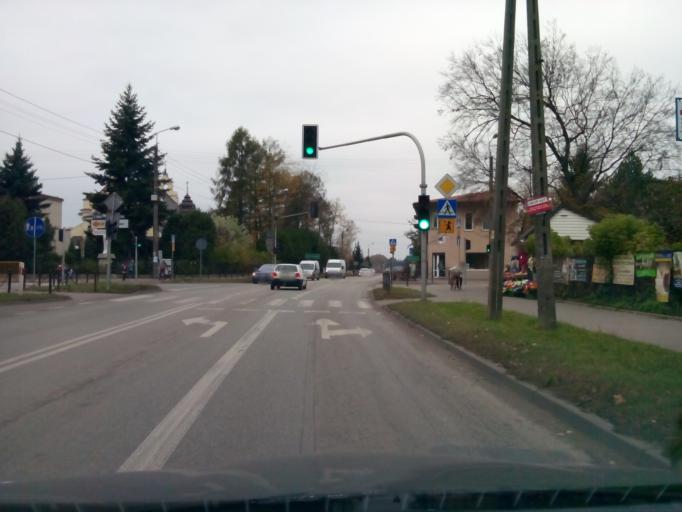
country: PL
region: Masovian Voivodeship
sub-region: Powiat zyrardowski
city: Radziejowice
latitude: 52.0861
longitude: 20.5532
